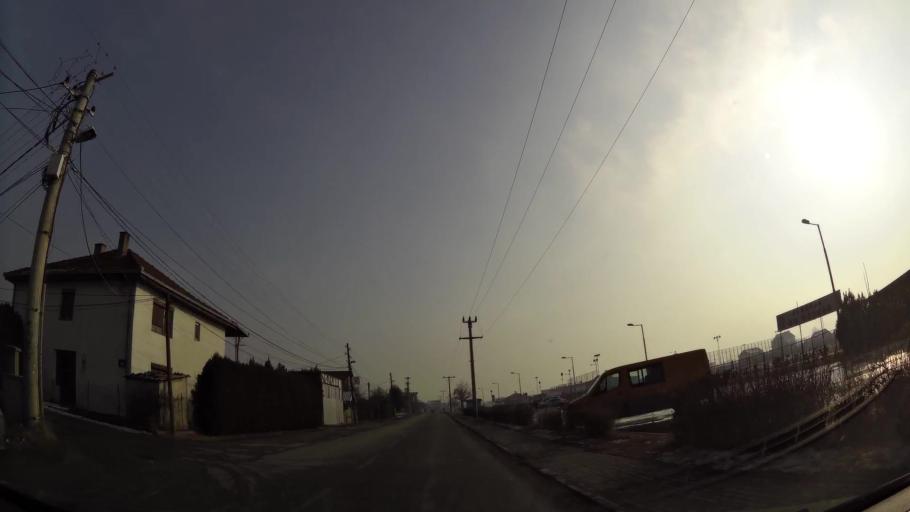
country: MK
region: Ilinden
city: Marino
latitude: 41.9884
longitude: 21.5876
